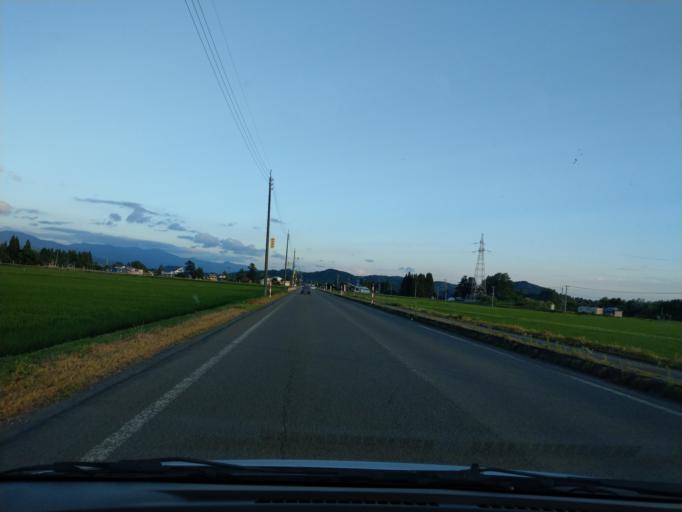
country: JP
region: Akita
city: Kakunodatemachi
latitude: 39.6309
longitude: 140.5704
